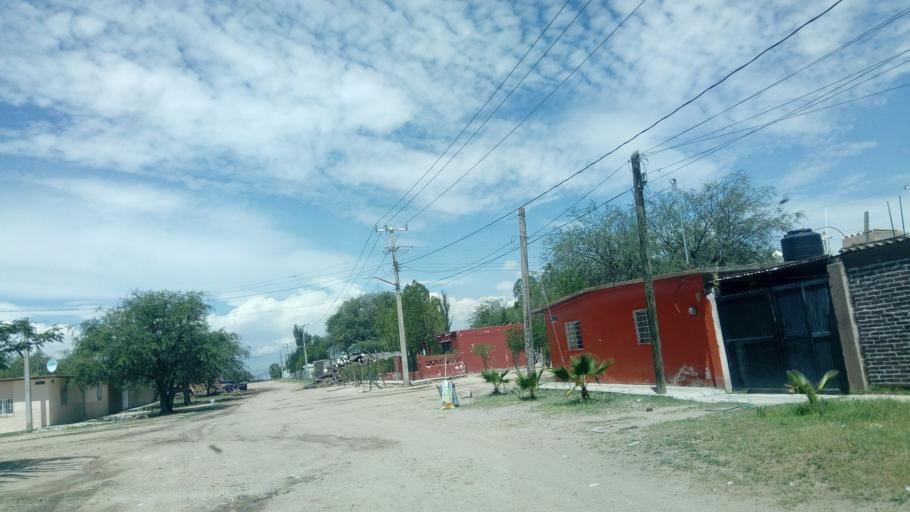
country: MX
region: Durango
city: Victoria de Durango
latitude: 24.0183
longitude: -104.5878
